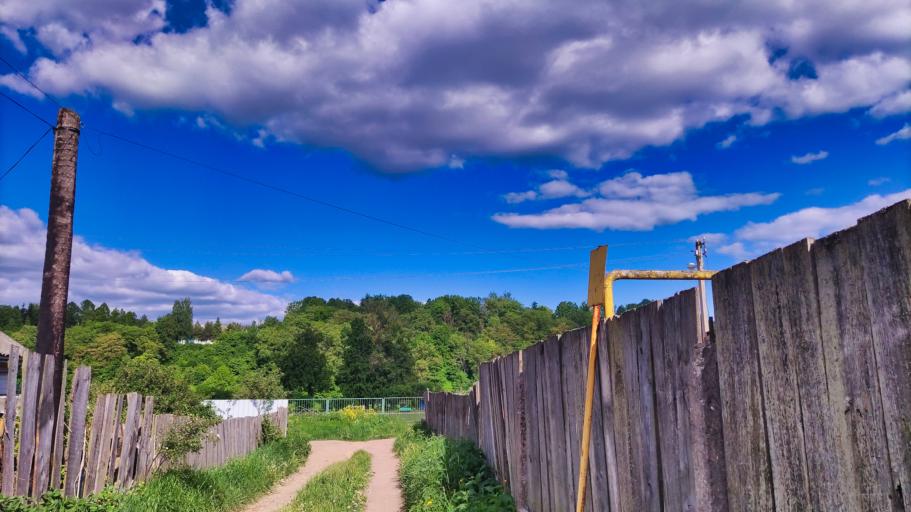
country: RU
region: Tverskaya
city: Rzhev
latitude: 56.2468
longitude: 34.3472
